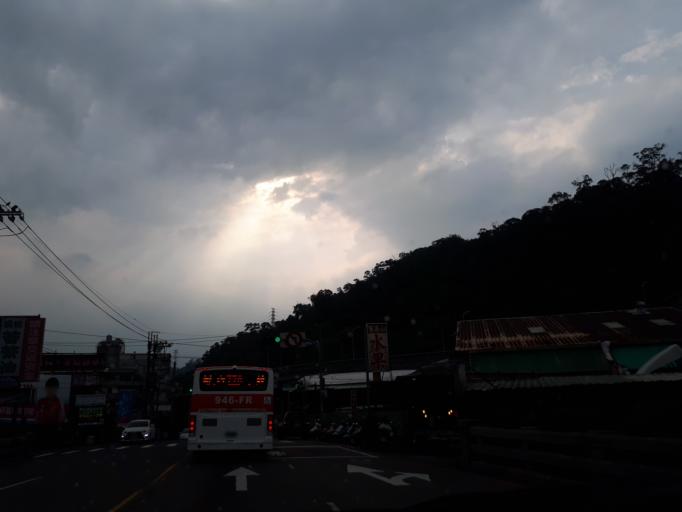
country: TW
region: Taipei
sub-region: Taipei
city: Banqiao
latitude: 24.9572
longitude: 121.5010
